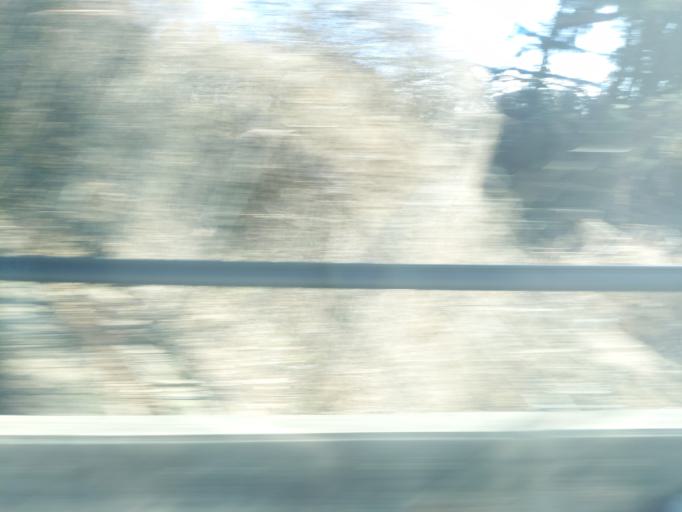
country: JP
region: Fukushima
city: Sukagawa
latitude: 37.3177
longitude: 140.3530
